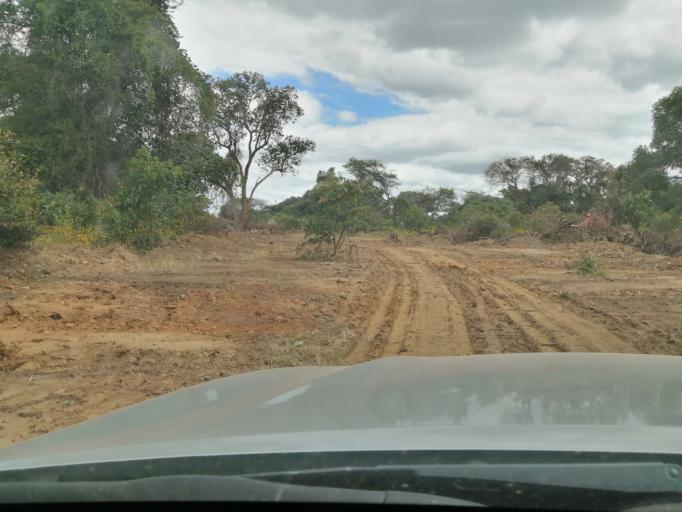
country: ZM
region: Central
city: Mumbwa
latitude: -14.5855
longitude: 27.1963
